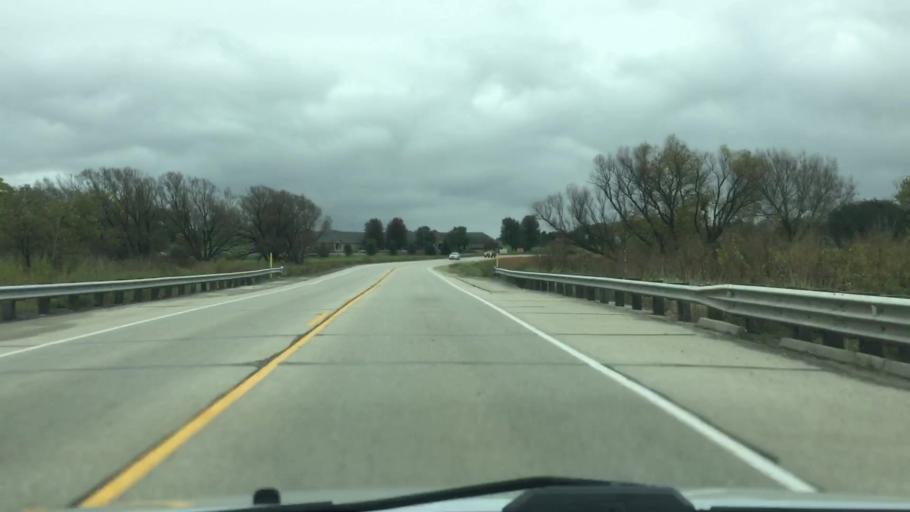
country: US
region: Wisconsin
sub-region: Walworth County
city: Elkhorn
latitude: 42.7345
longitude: -88.5451
